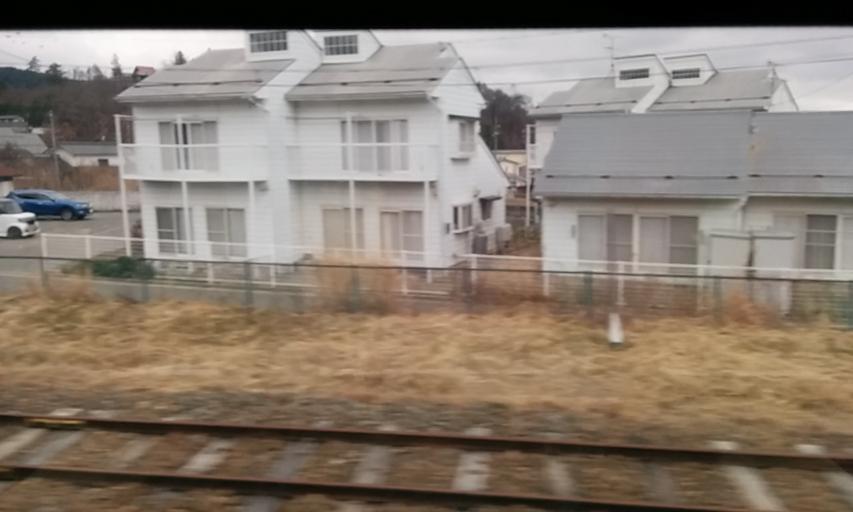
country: JP
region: Nagano
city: Hotaka
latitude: 36.4016
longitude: 138.0135
